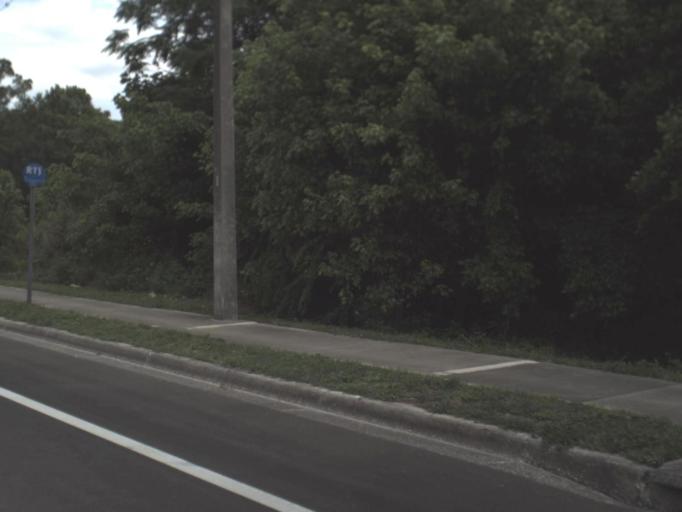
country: US
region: Florida
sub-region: Alachua County
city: Gainesville
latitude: 29.6439
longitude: -82.2912
